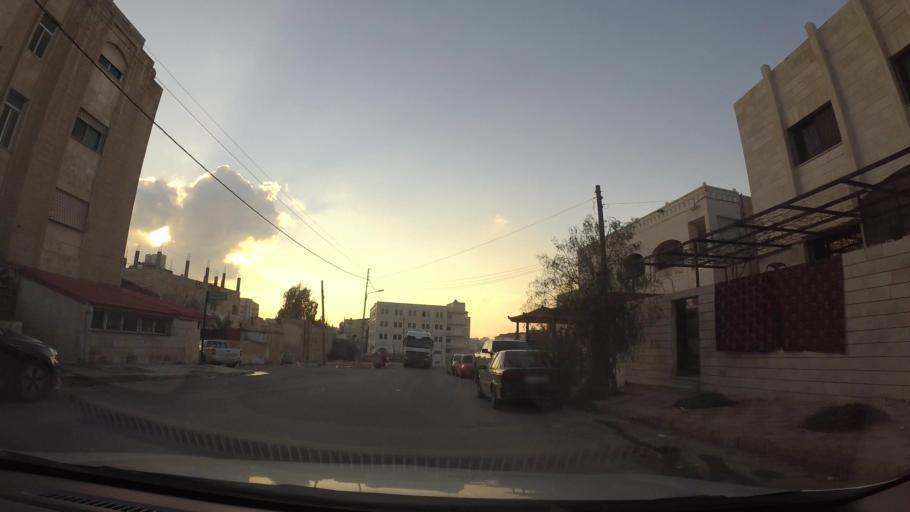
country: JO
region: Amman
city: Al Bunayyat ash Shamaliyah
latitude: 31.9096
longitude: 35.9147
